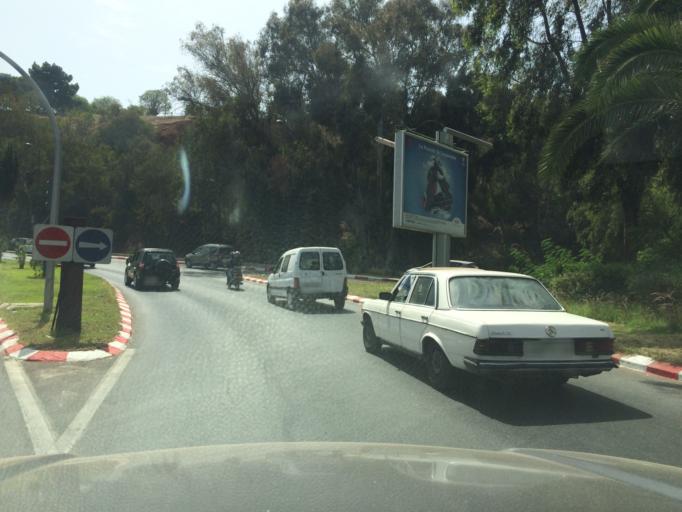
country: MA
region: Rabat-Sale-Zemmour-Zaer
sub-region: Rabat
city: Rabat
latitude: 34.0197
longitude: -6.8191
